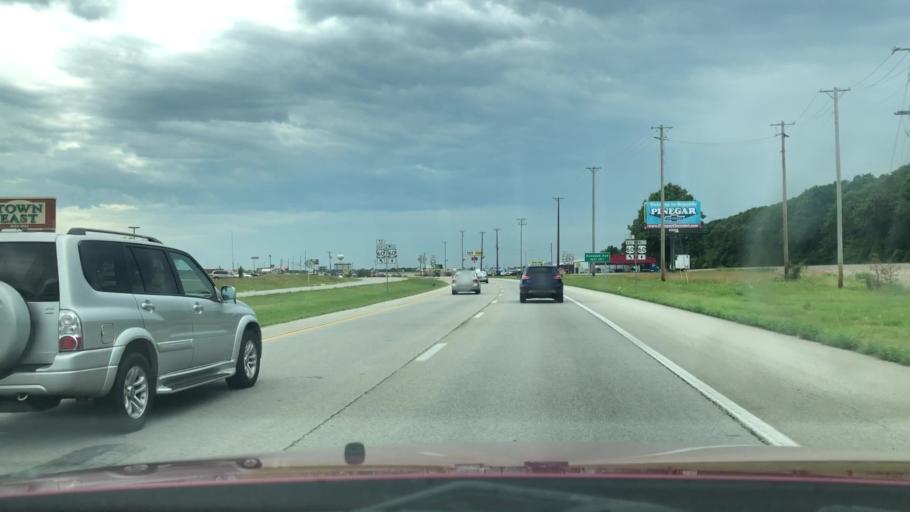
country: US
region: Missouri
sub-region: Greene County
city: Republic
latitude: 37.1358
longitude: -93.4529
